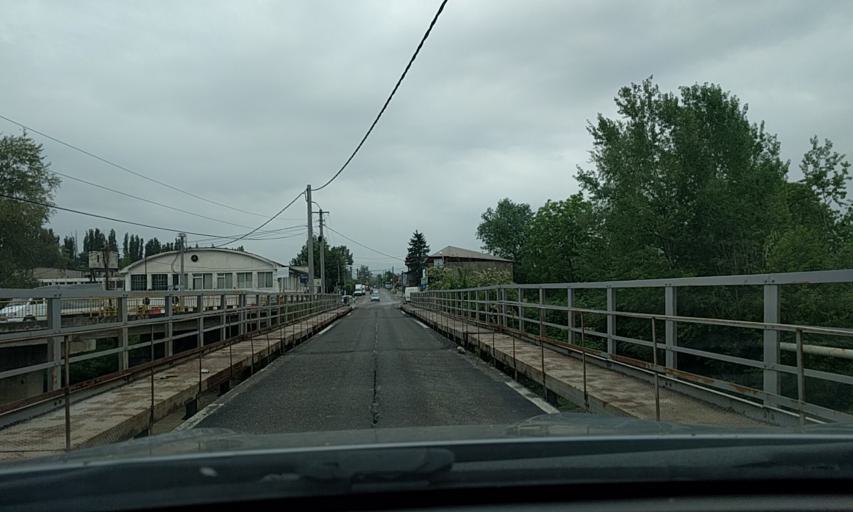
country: RO
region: Dambovita
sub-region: Oras Pucioasa
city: Glodeni
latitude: 45.0439
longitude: 25.4392
